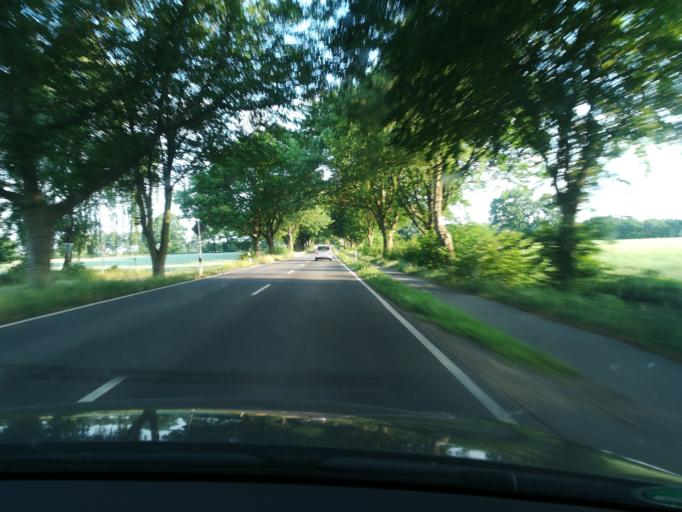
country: DE
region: Schleswig-Holstein
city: Grossensee
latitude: 53.6255
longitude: 10.3269
